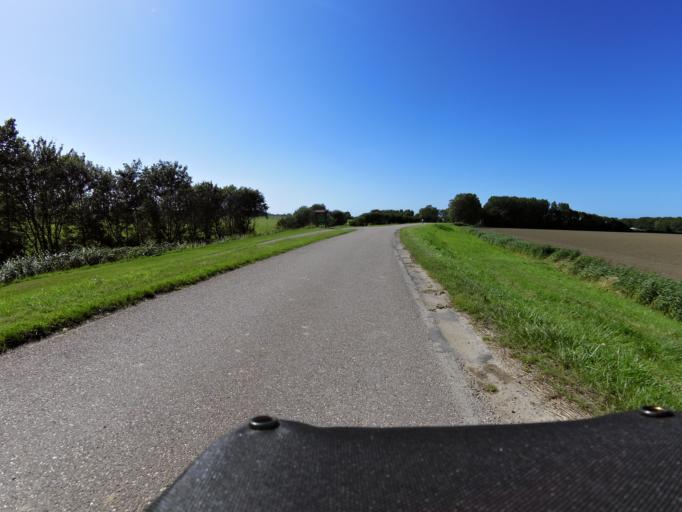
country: NL
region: South Holland
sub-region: Gemeente Goeree-Overflakkee
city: Dirksland
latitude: 51.7744
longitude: 4.0581
